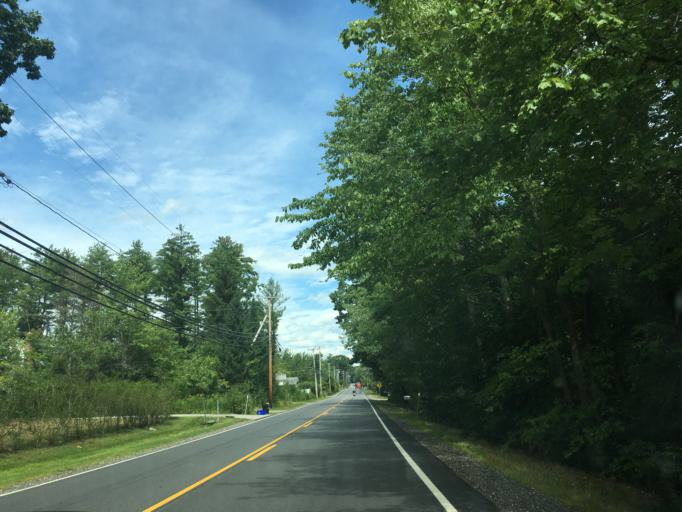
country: US
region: New Hampshire
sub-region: Rockingham County
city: Exeter
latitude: 42.9661
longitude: -70.9540
